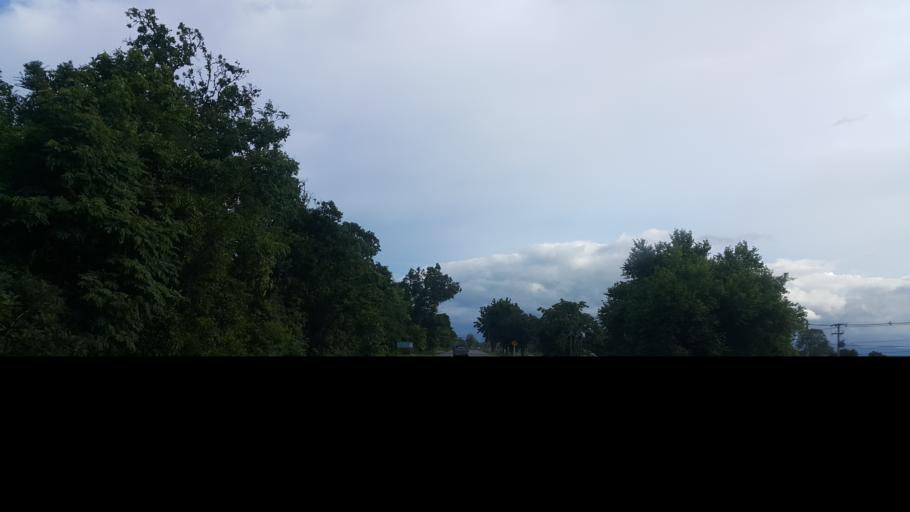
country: TH
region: Tak
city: Ban Tak
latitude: 17.1008
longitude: 99.0746
